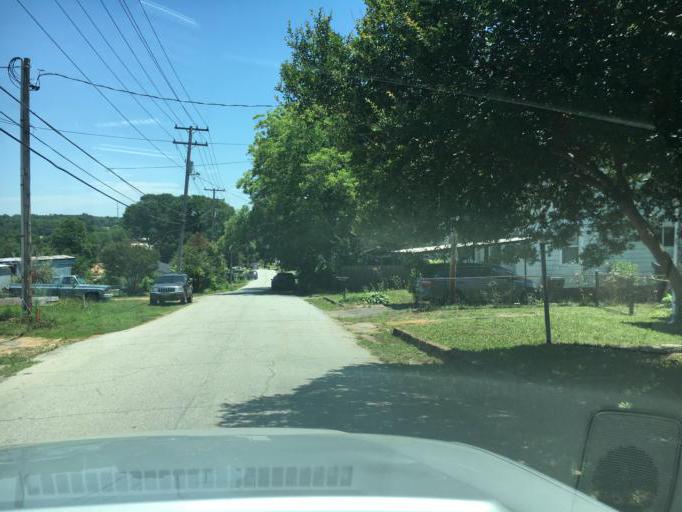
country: US
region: South Carolina
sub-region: Greenville County
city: Greer
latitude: 34.9629
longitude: -82.2118
